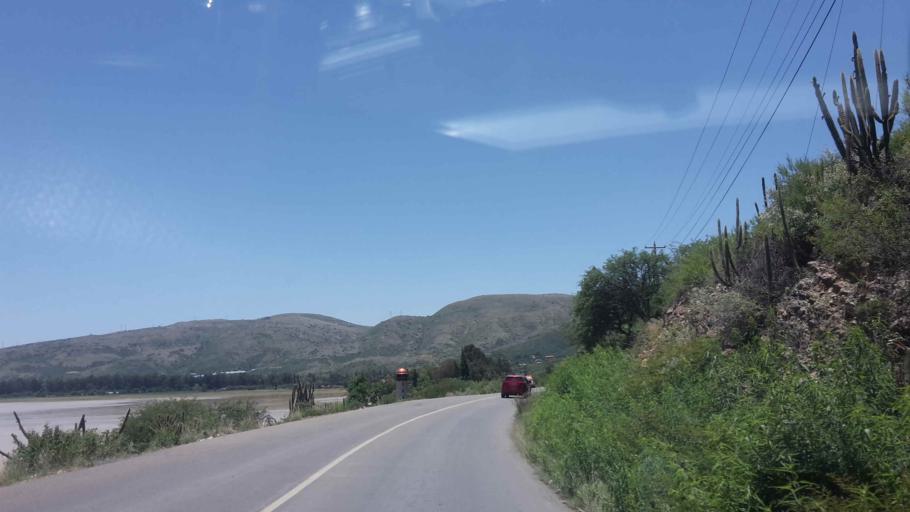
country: BO
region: Cochabamba
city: Tarata
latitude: -17.5315
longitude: -66.0907
